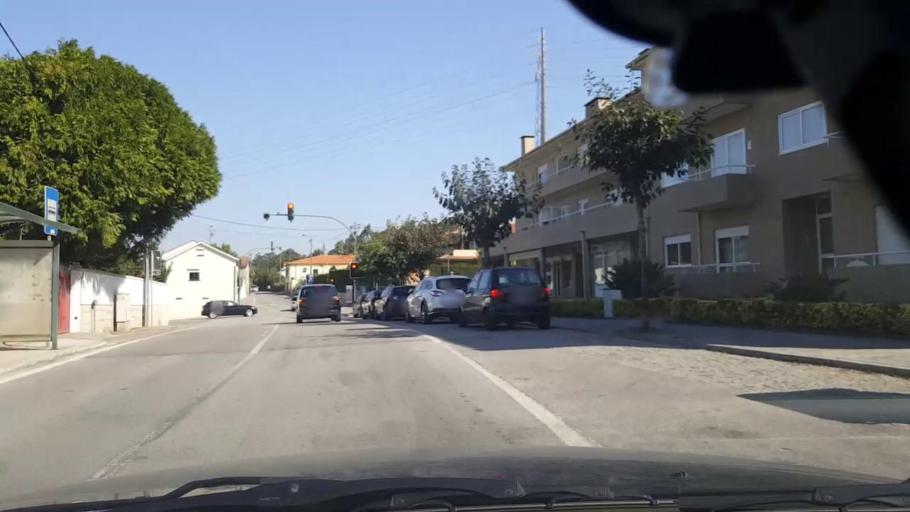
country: PT
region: Porto
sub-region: Vila do Conde
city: Arvore
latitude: 41.3105
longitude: -8.6791
